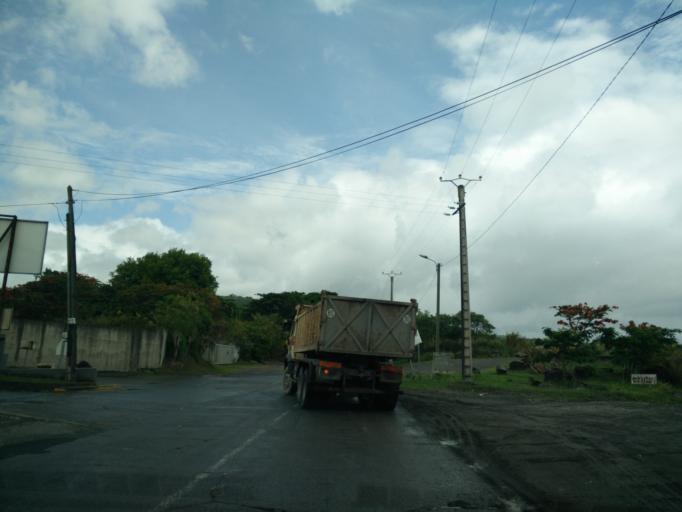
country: MQ
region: Martinique
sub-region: Martinique
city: Saint-Pierre
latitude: 14.7554
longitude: -61.1833
